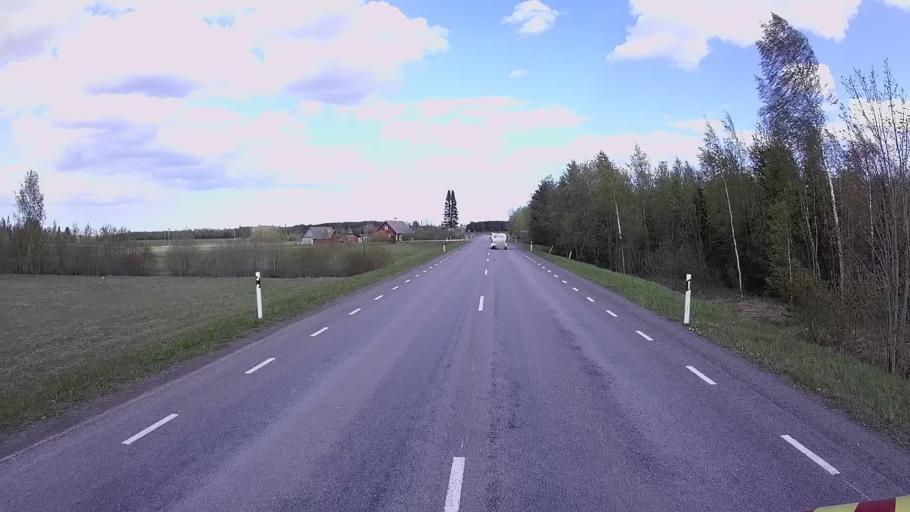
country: EE
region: Tartu
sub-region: Alatskivi vald
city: Kallaste
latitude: 58.5152
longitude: 26.9850
